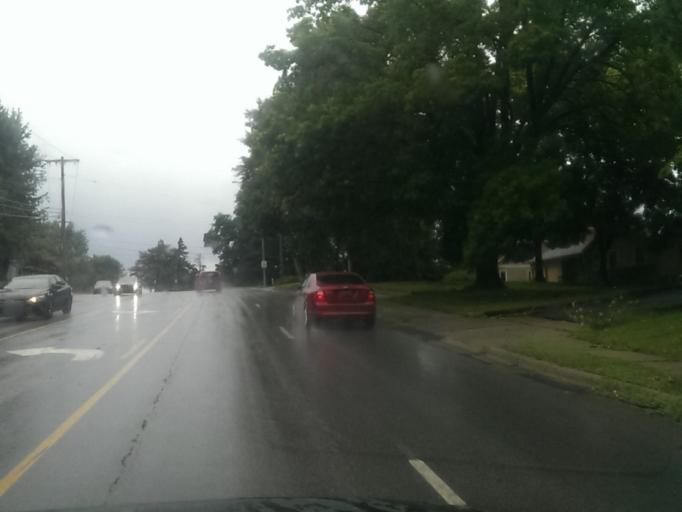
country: US
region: Kansas
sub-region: Johnson County
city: Leawood
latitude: 38.9325
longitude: -94.5828
